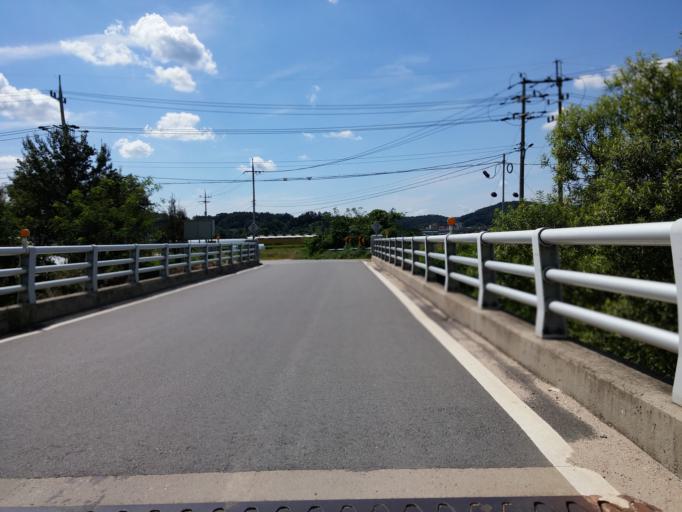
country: KR
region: Chungcheongbuk-do
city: Cheongju-si
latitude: 36.5850
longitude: 127.5013
